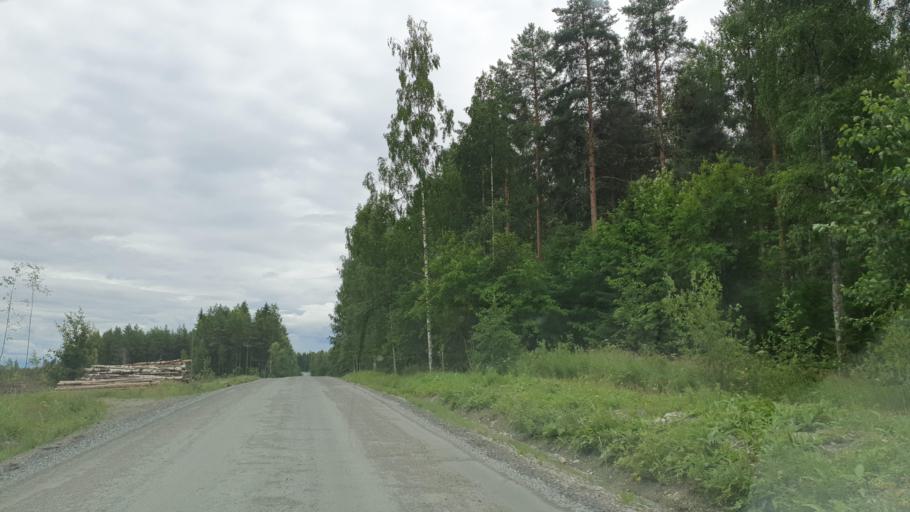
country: FI
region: Northern Savo
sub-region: Ylae-Savo
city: Iisalmi
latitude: 63.5246
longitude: 27.0922
